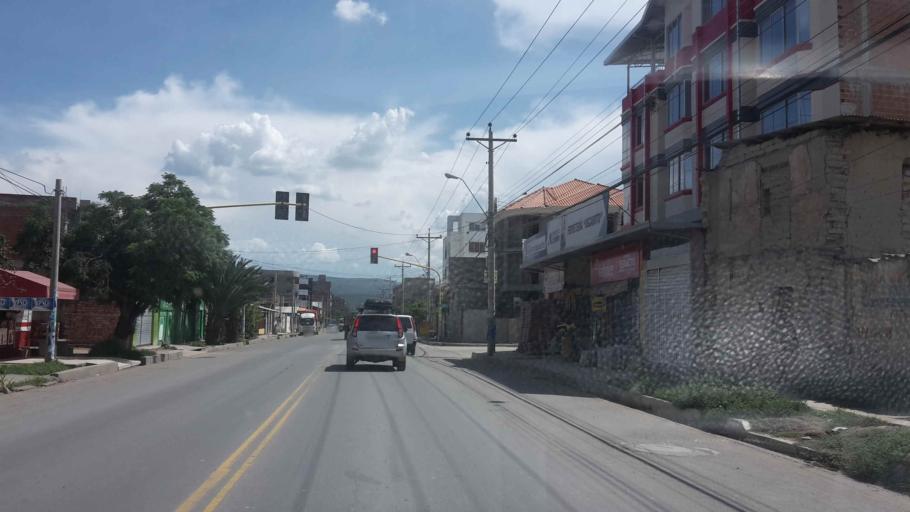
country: BO
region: Cochabamba
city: Cochabamba
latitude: -17.3843
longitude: -66.2366
